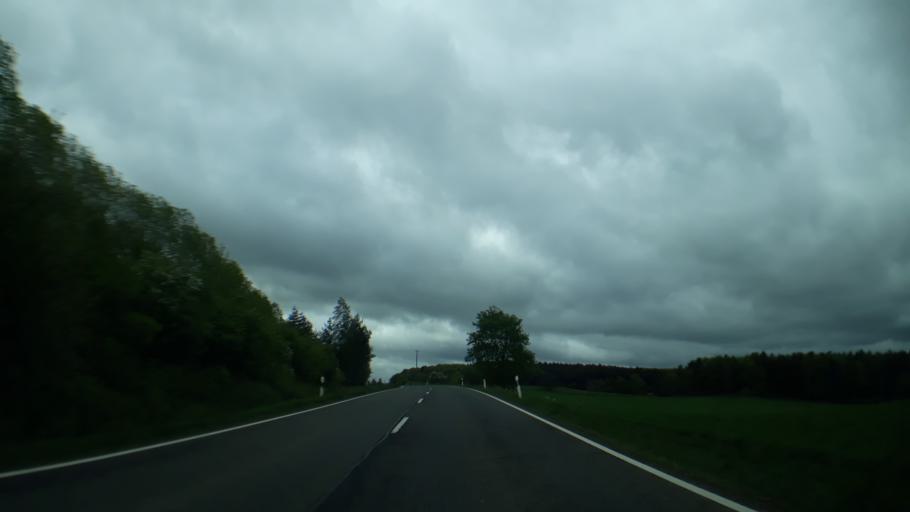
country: DE
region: North Rhine-Westphalia
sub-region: Regierungsbezirk Koln
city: Kall
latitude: 50.5284
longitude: 6.5867
